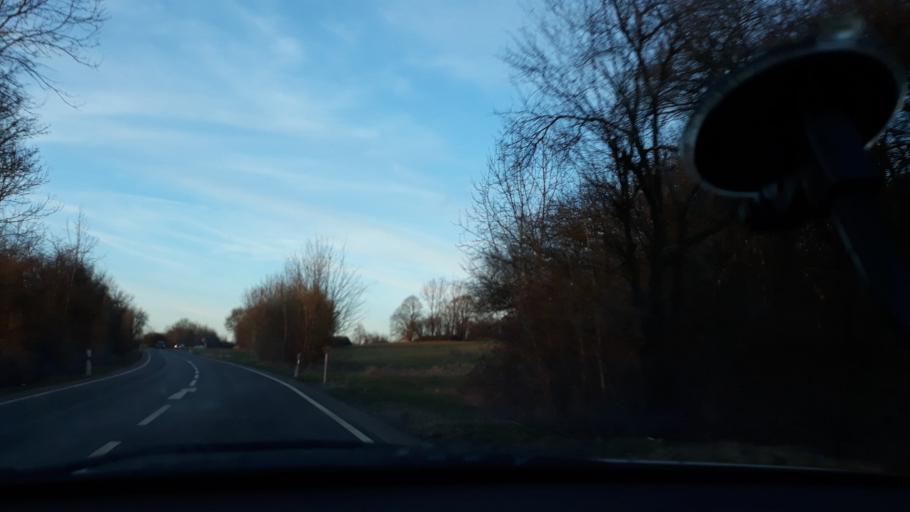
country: DE
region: Saarland
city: Sankt Ingbert
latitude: 49.2299
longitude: 7.1203
